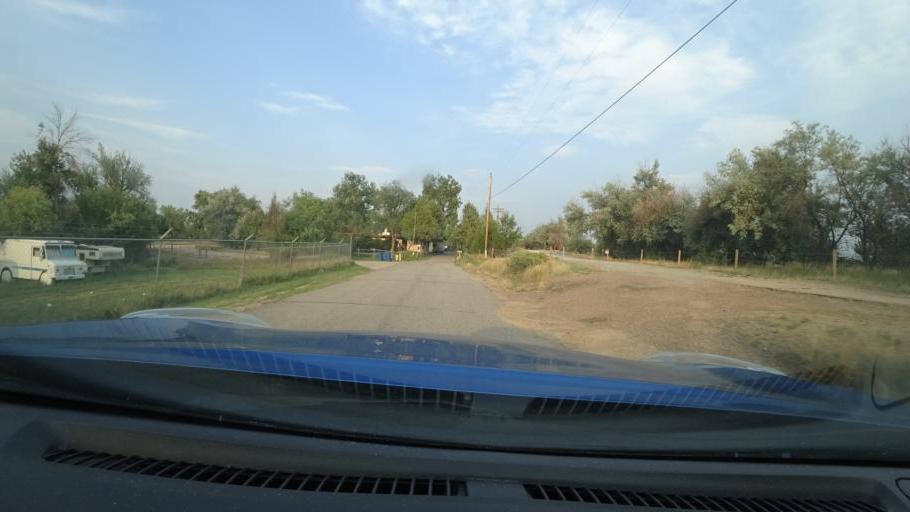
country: US
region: Colorado
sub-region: Adams County
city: Aurora
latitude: 39.7365
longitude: -104.7781
